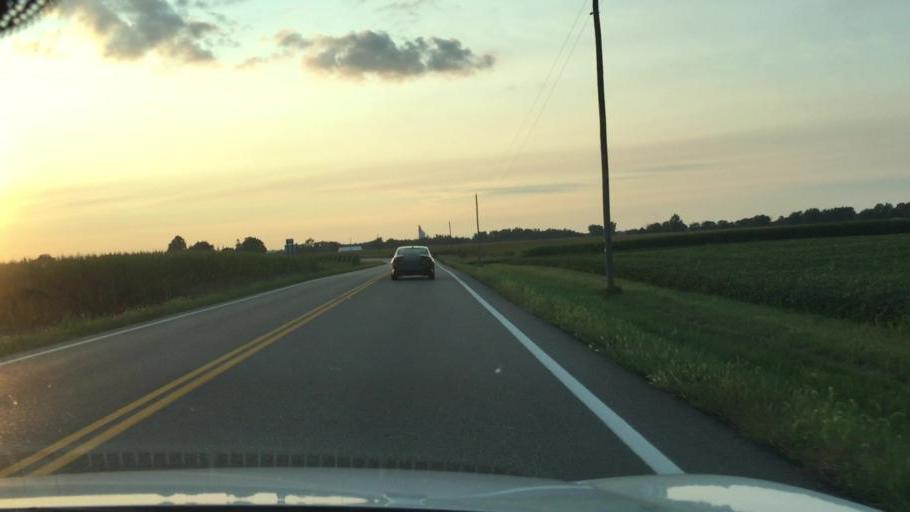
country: US
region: Ohio
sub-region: Champaign County
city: Mechanicsburg
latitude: 40.0589
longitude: -83.5357
